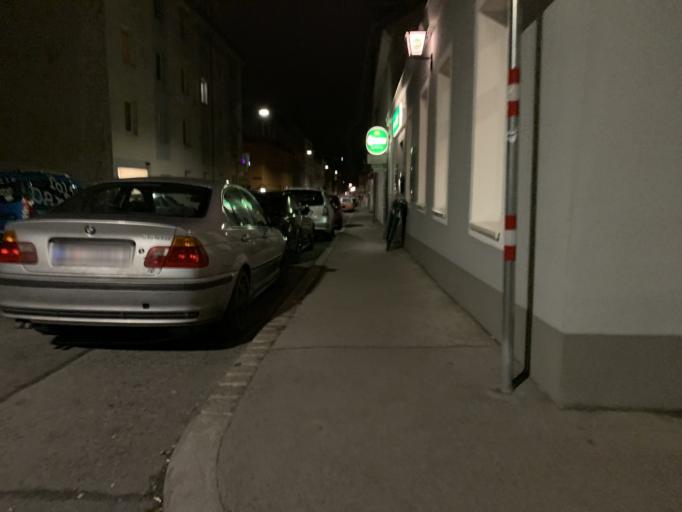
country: AT
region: Vienna
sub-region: Wien Stadt
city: Vienna
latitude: 48.1791
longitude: 16.3367
